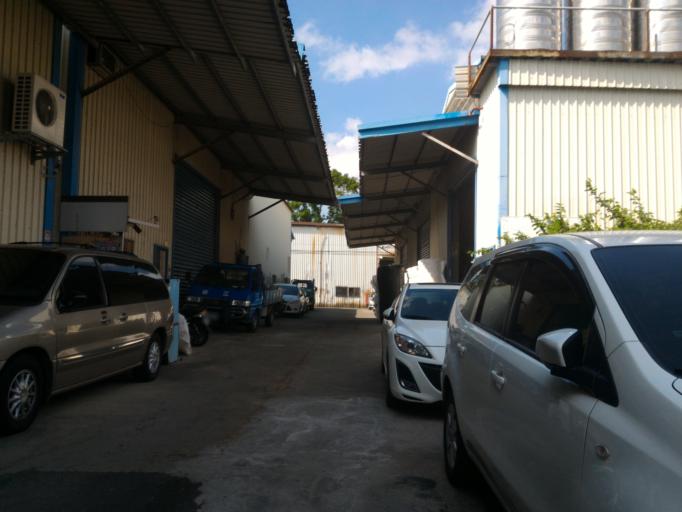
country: TW
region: Taiwan
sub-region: Taoyuan
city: Taoyuan
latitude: 24.9577
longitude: 121.3975
